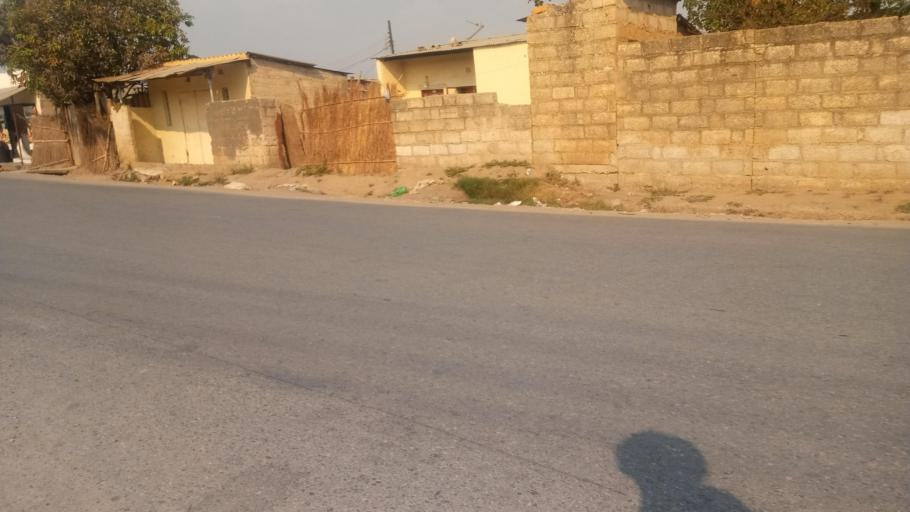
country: ZM
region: Lusaka
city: Lusaka
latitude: -15.4398
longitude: 28.3783
